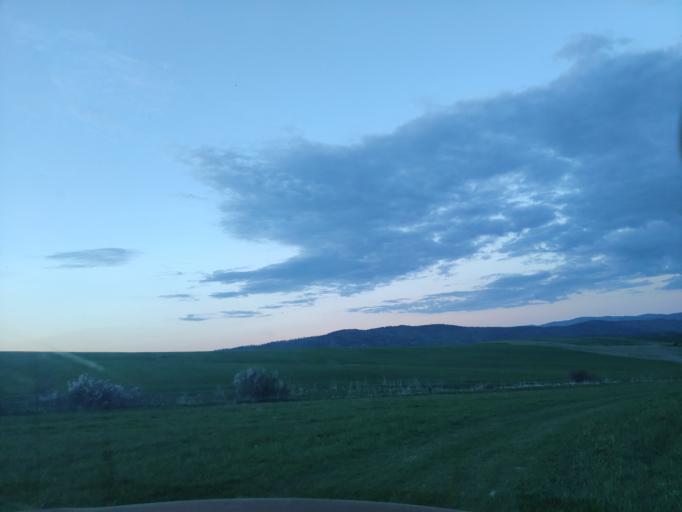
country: SK
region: Presovsky
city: Lipany
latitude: 49.1810
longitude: 20.8157
